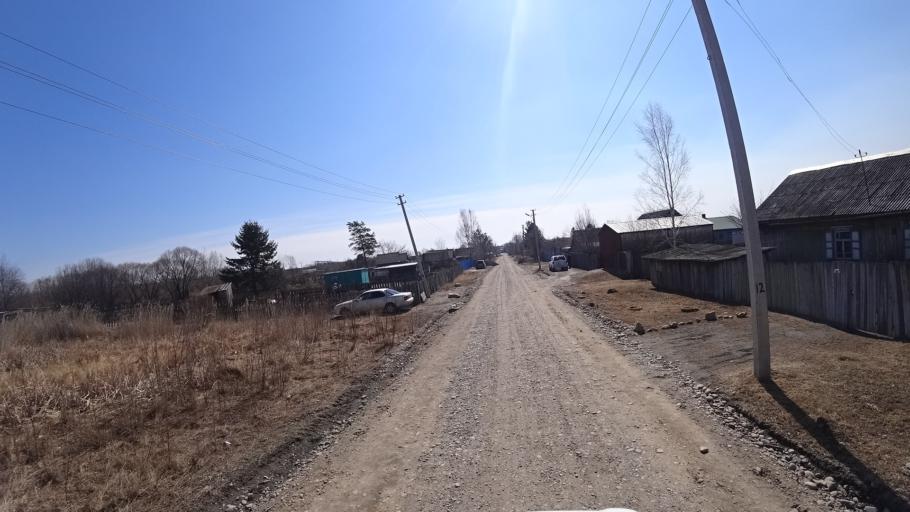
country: RU
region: Amur
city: Novobureyskiy
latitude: 49.7907
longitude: 129.8526
